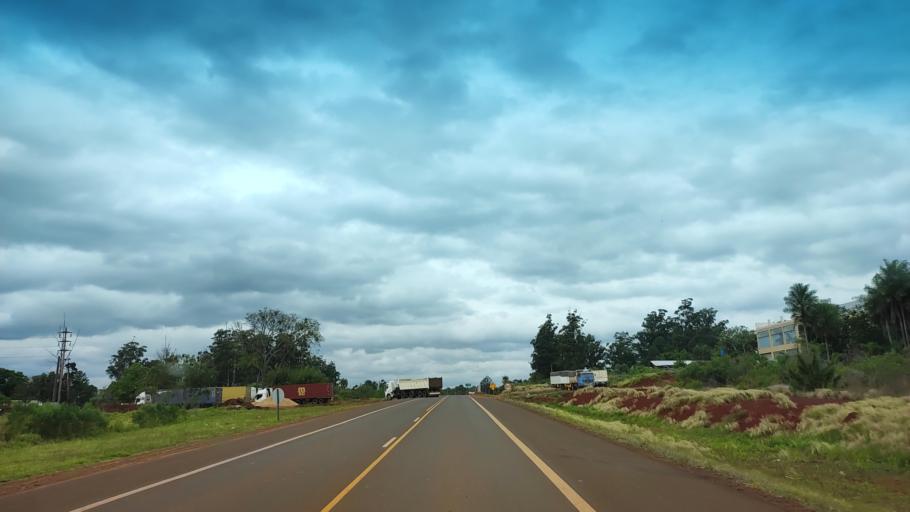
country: AR
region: Misiones
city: Garupa
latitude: -27.4635
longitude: -55.8700
